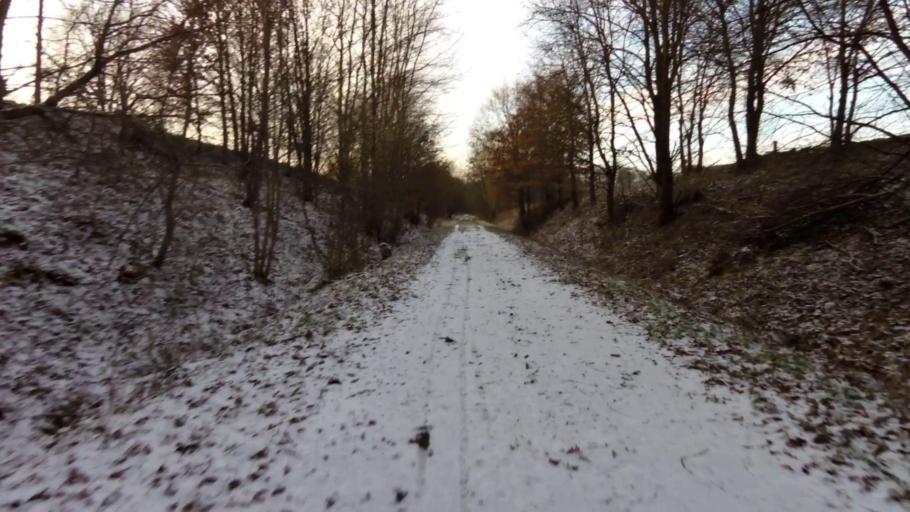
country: PL
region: West Pomeranian Voivodeship
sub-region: Powiat swidwinski
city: Polczyn-Zdroj
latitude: 53.6580
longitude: 16.0339
